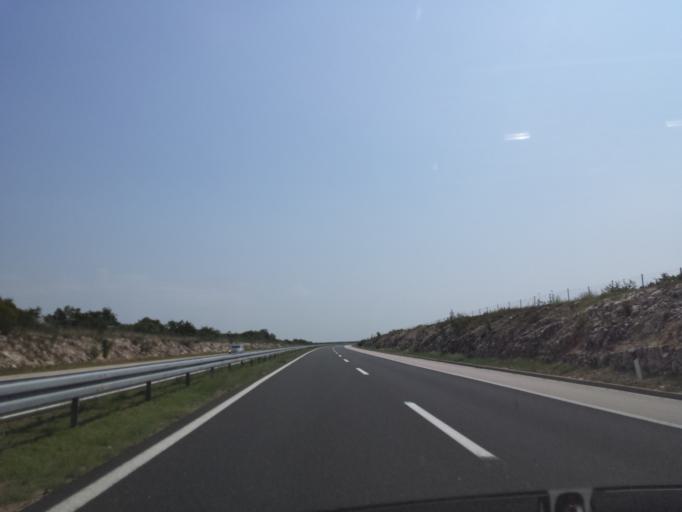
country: HR
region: Zadarska
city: Polaca
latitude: 44.0875
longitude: 15.4978
